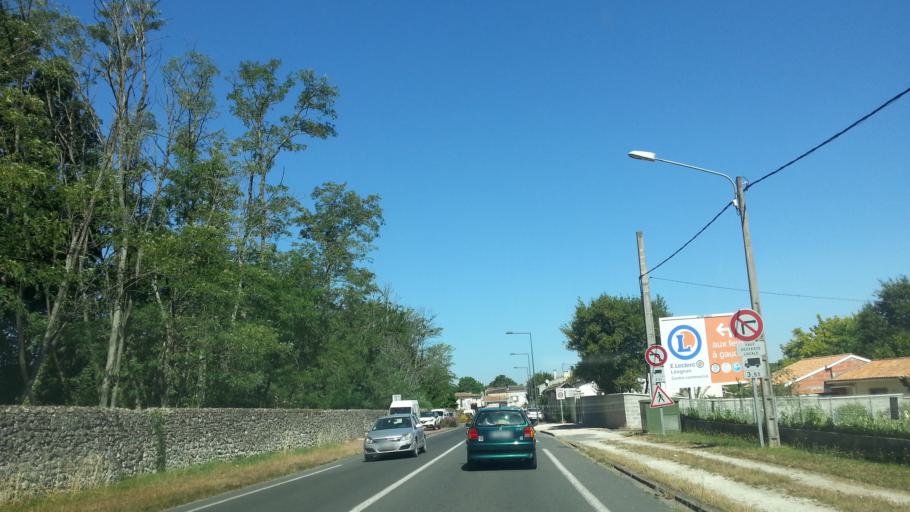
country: FR
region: Aquitaine
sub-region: Departement de la Gironde
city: Cadaujac
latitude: 44.7489
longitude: -0.5466
